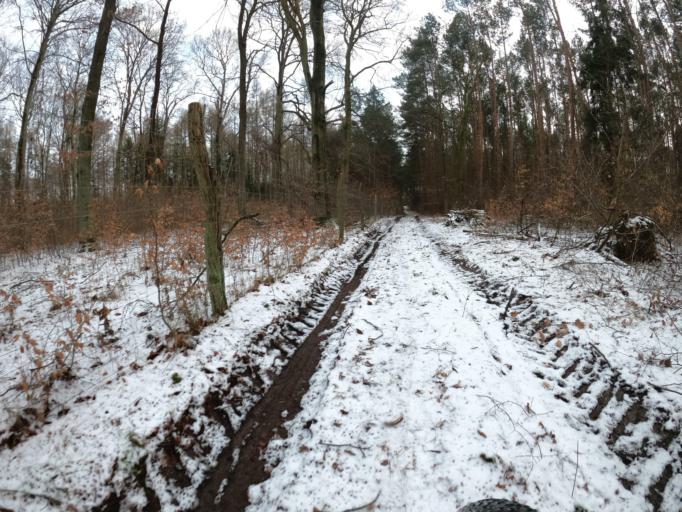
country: PL
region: Lubusz
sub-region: Powiat slubicki
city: Cybinka
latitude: 52.1935
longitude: 14.8690
